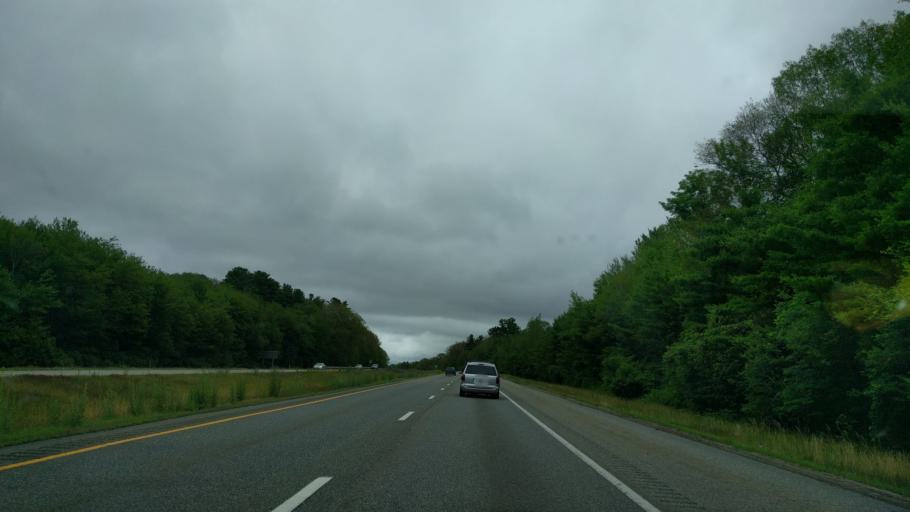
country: US
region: Massachusetts
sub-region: Worcester County
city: Millville
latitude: 42.0183
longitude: -71.5959
